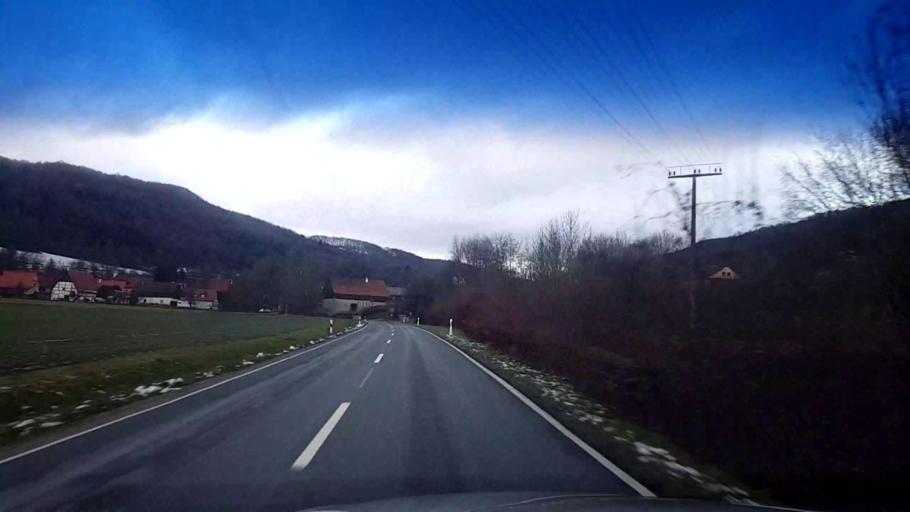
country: DE
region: Bavaria
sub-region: Upper Franconia
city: Buttenheim
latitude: 49.8287
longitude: 11.0788
